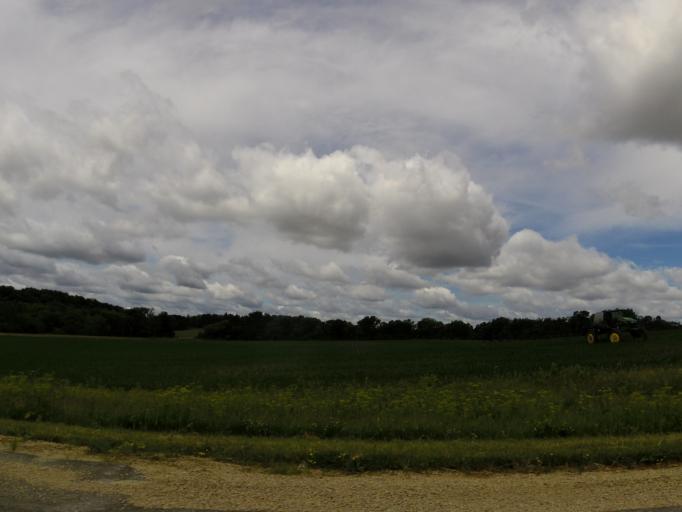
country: US
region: Minnesota
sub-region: Mower County
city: Grand Meadow
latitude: 43.7481
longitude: -92.4792
